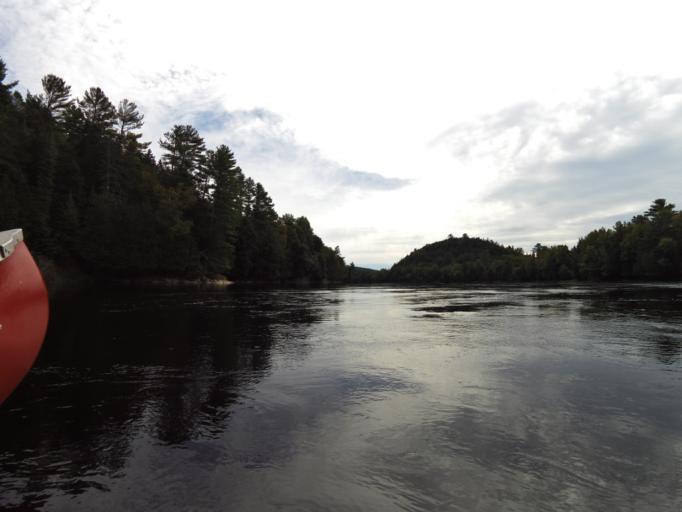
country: CA
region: Quebec
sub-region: Outaouais
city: Wakefield
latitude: 45.7683
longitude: -75.9327
